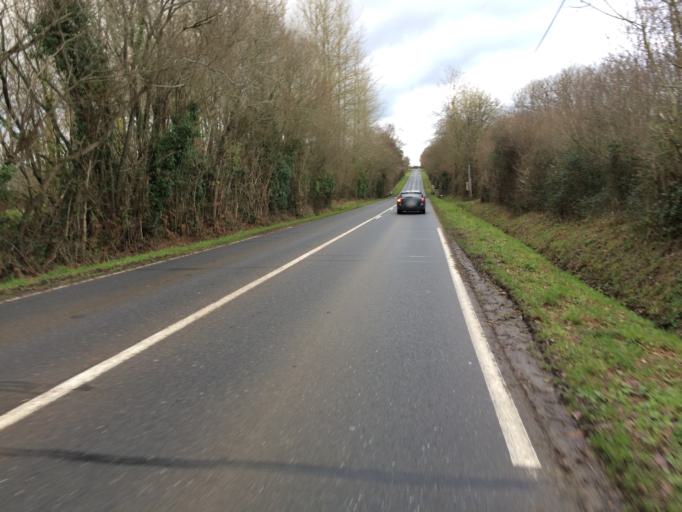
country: FR
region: Brittany
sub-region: Departement du Finistere
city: Daoulas
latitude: 48.3410
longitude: -4.2594
